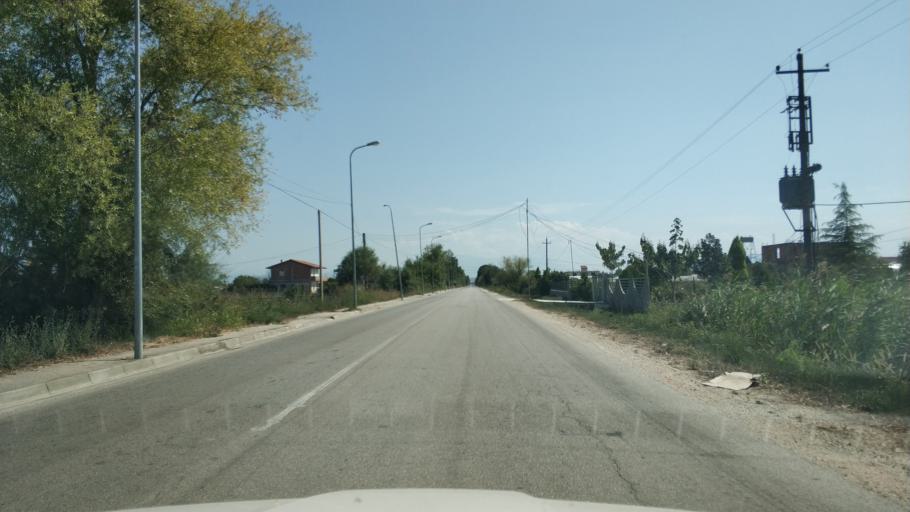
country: AL
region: Fier
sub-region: Rrethi i Lushnjes
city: Krutja e Poshtme
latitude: 40.8888
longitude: 19.6449
